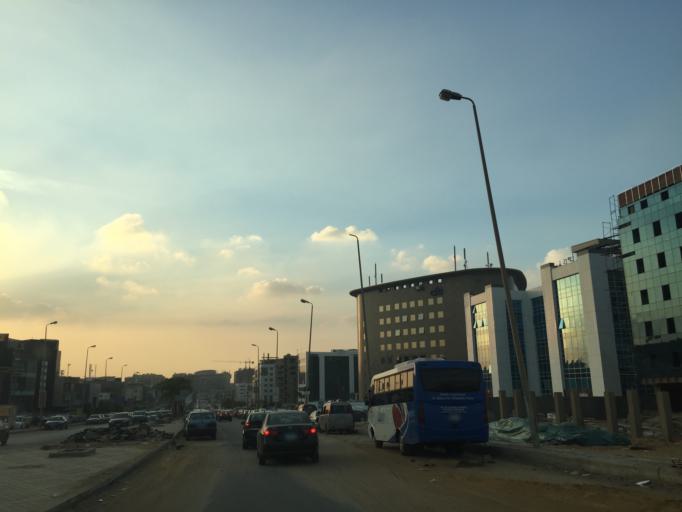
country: EG
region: Muhafazat al Qahirah
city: Cairo
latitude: 30.0199
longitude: 31.4256
